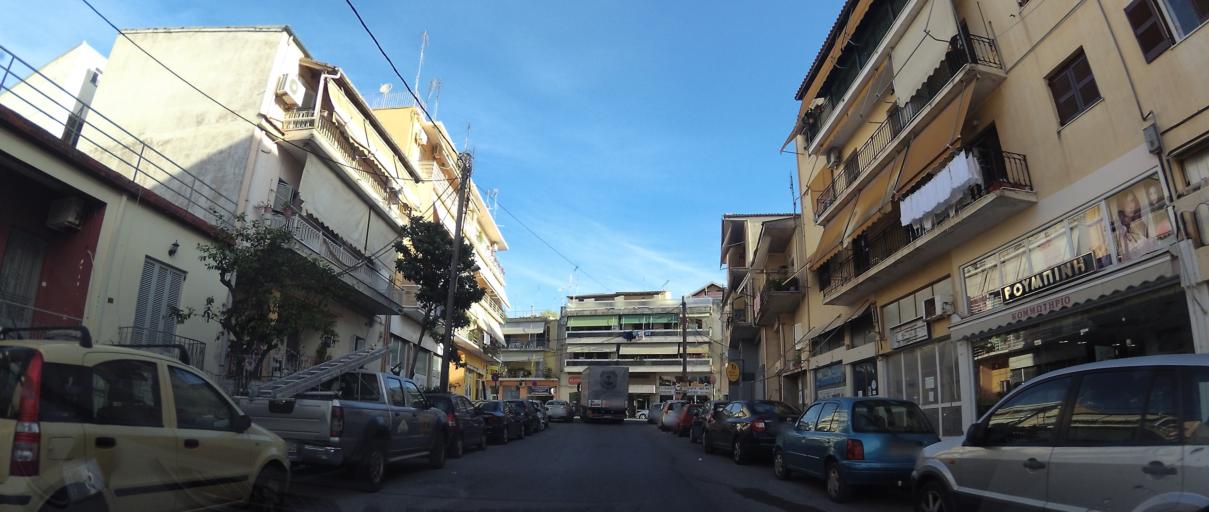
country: GR
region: Ionian Islands
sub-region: Nomos Kerkyras
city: Kerkyra
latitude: 39.6215
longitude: 19.9117
